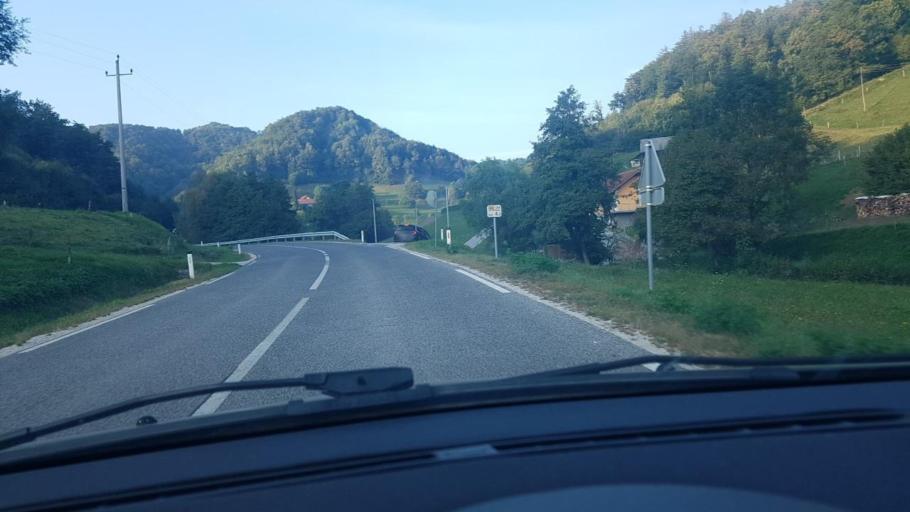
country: SI
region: Rogatec
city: Rogatec
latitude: 46.2579
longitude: 15.7026
